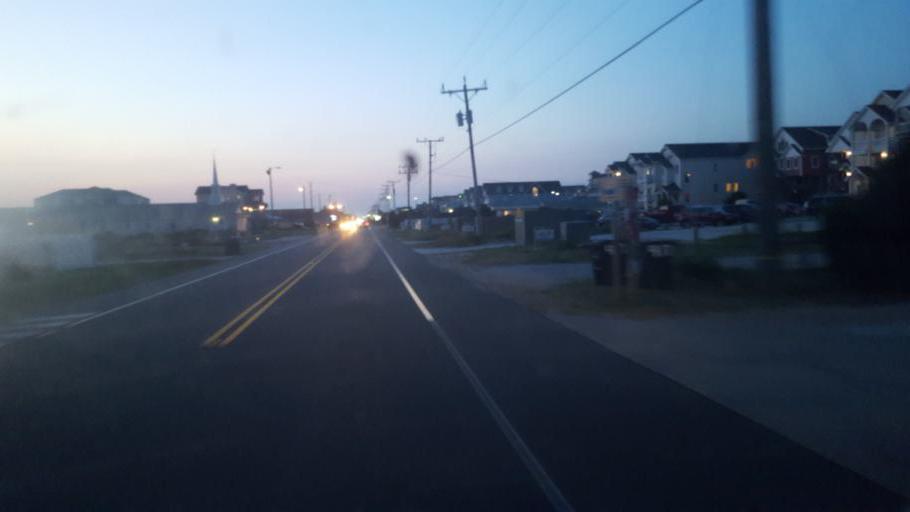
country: US
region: North Carolina
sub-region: Dare County
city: Kill Devil Hills
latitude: 36.0081
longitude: -75.6537
